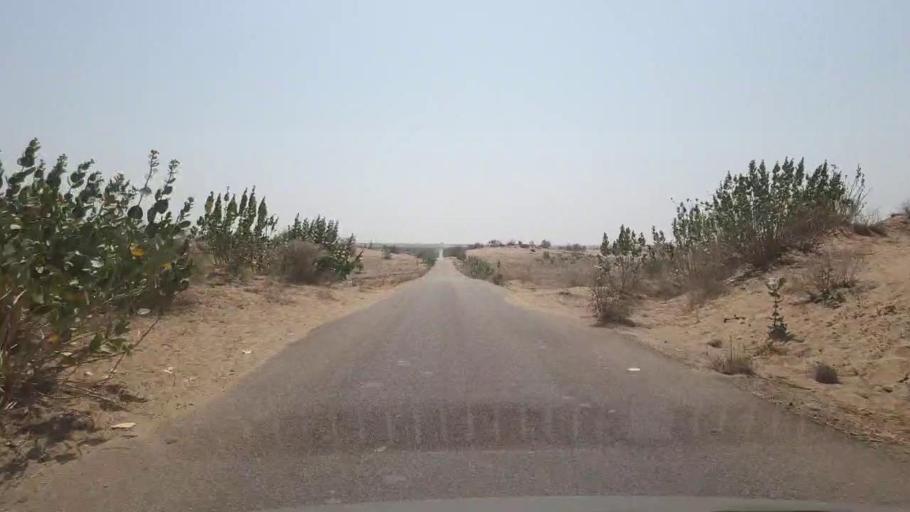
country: PK
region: Sindh
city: Chor
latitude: 25.6025
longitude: 70.1802
